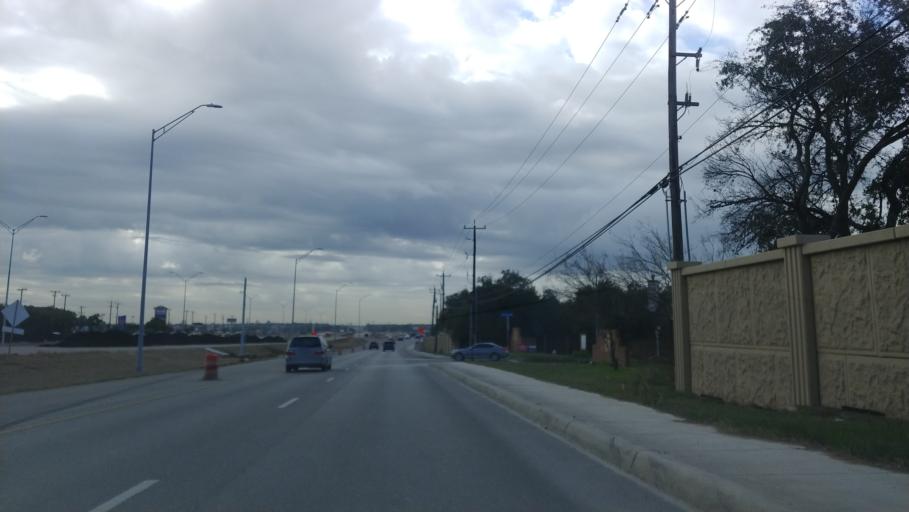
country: US
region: Texas
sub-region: Bexar County
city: Leon Valley
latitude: 29.4433
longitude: -98.7118
